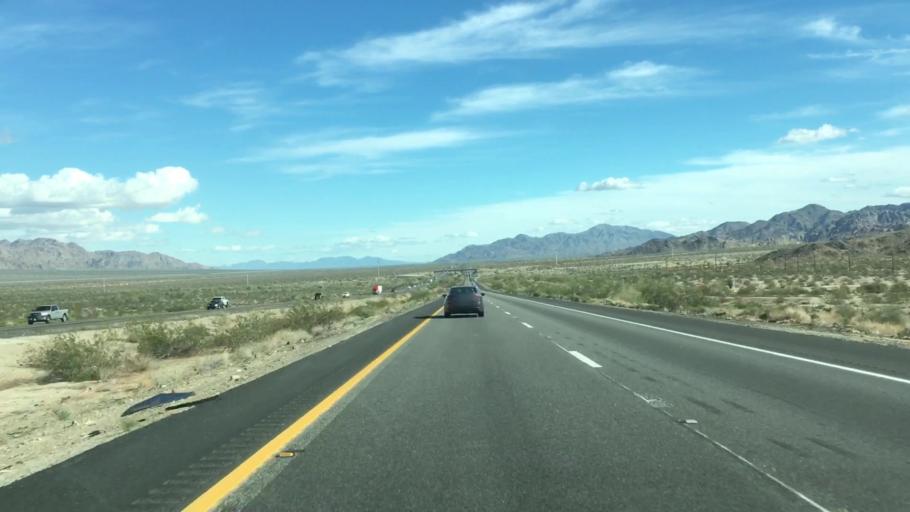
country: US
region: California
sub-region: Riverside County
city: Mecca
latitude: 33.6669
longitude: -115.6709
